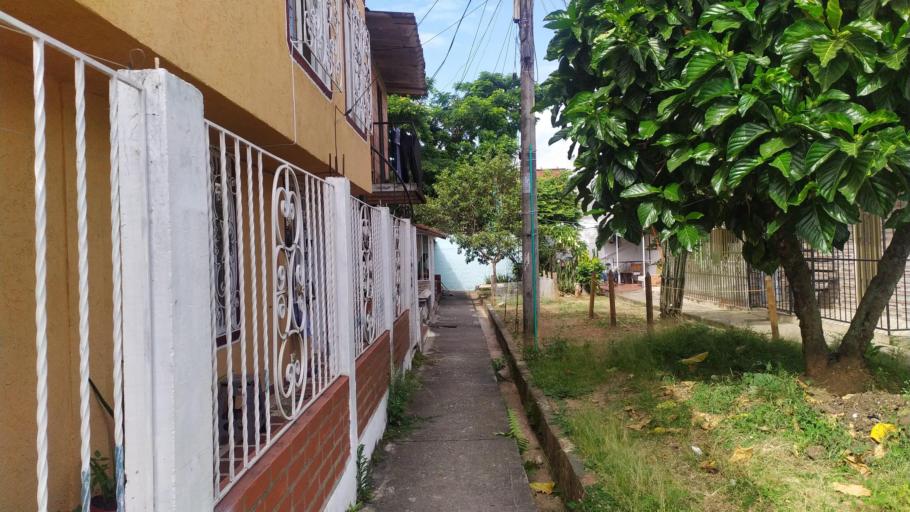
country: CO
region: Valle del Cauca
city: Jamundi
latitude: 3.2540
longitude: -76.5439
